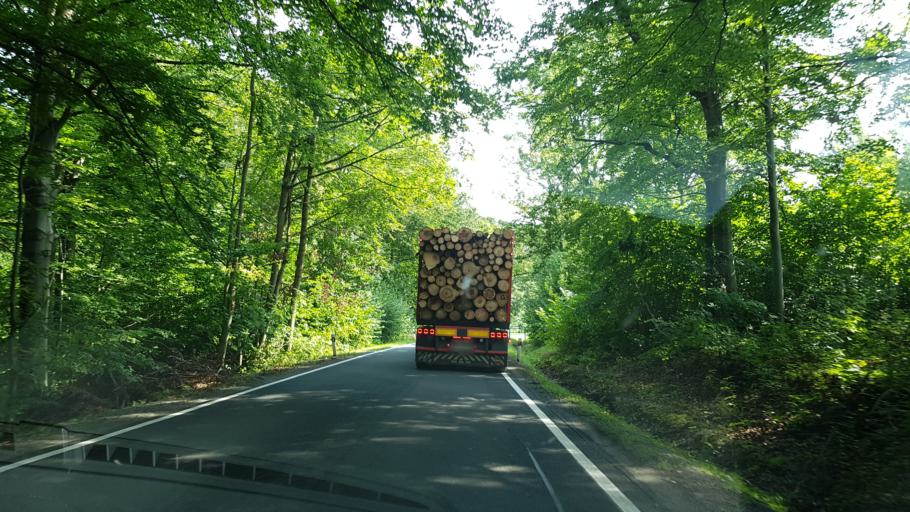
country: CZ
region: Olomoucky
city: Zlate Hory
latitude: 50.2395
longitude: 17.3410
